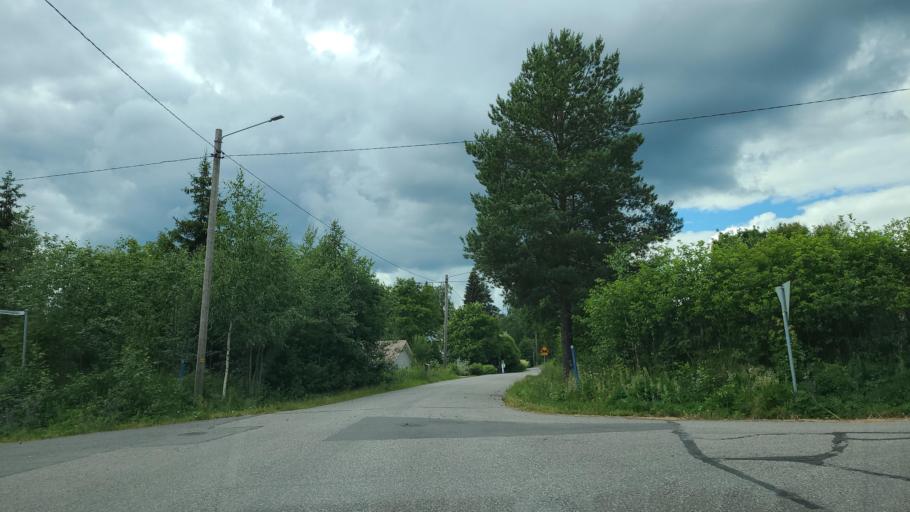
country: FI
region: Northern Savo
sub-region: Koillis-Savo
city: Kaavi
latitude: 62.9722
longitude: 28.4827
